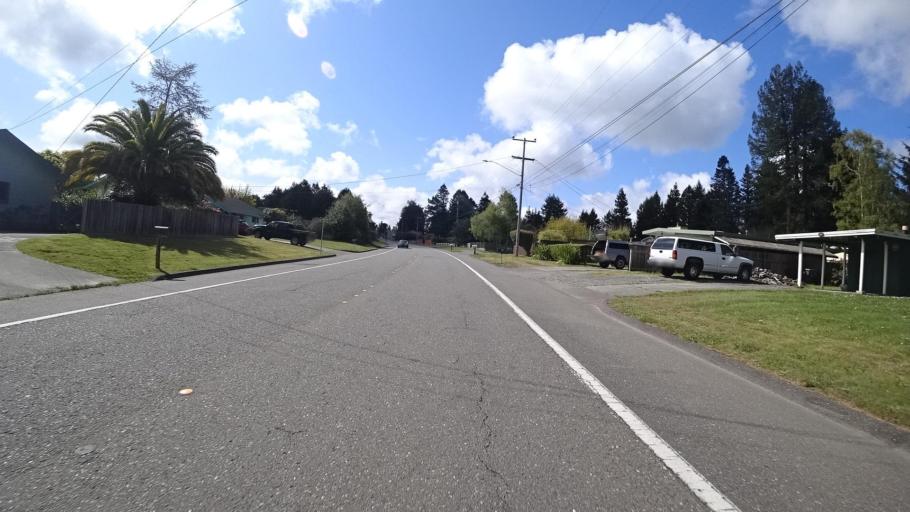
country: US
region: California
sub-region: Humboldt County
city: Pine Hills
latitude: 40.7468
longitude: -124.1478
